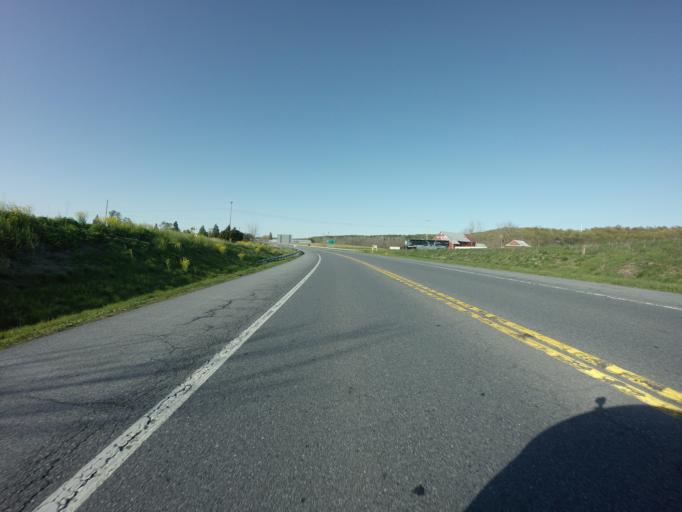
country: US
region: Maryland
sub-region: Frederick County
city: Woodsboro
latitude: 39.5235
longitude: -77.3136
